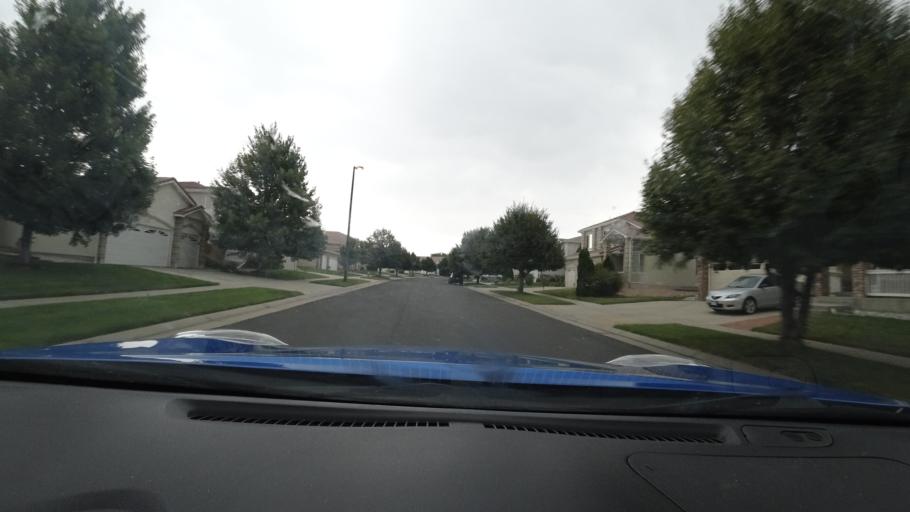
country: US
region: Colorado
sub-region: Adams County
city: Aurora
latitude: 39.7836
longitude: -104.7474
